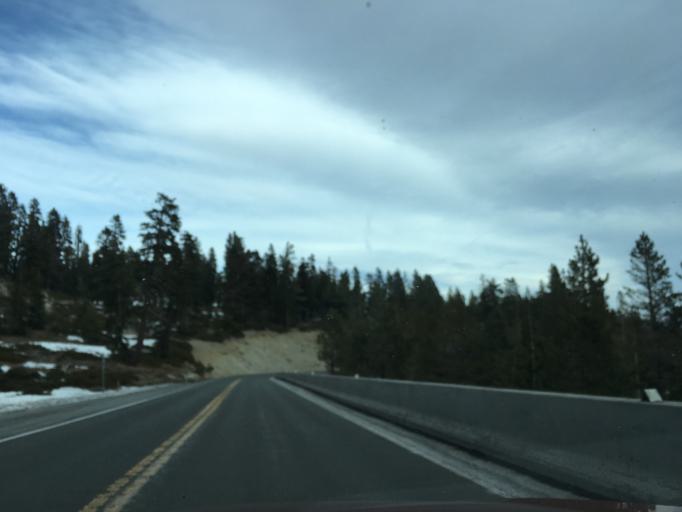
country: US
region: Nevada
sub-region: Washoe County
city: Incline Village
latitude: 39.3287
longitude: -119.8814
